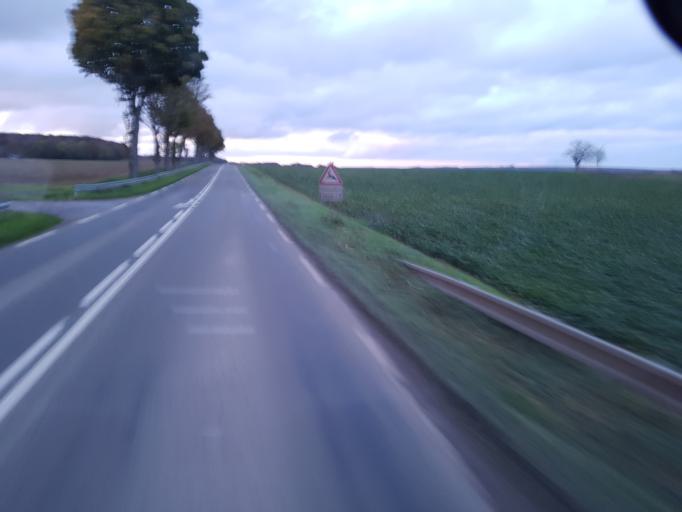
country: FR
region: Picardie
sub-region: Departement de l'Aisne
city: Coincy
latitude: 49.1571
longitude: 3.3848
